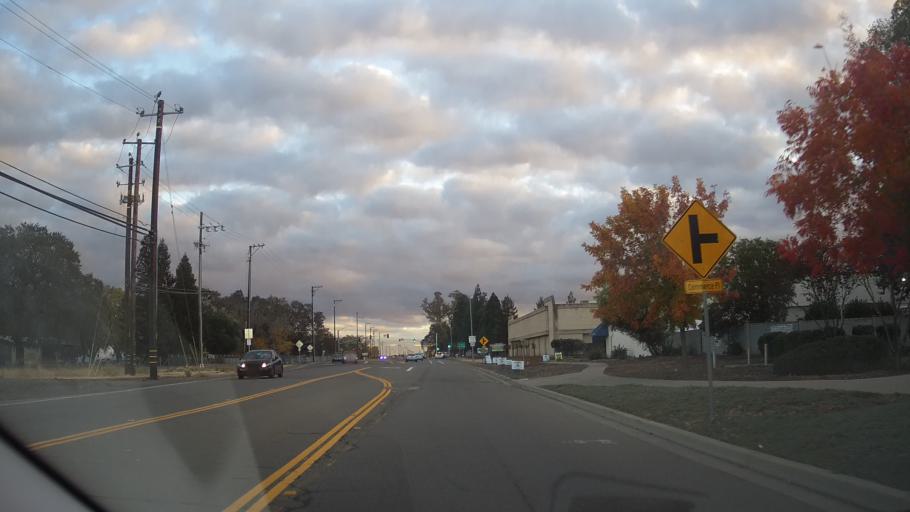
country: US
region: California
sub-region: Solano County
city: Vacaville
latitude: 38.3539
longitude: -121.9341
